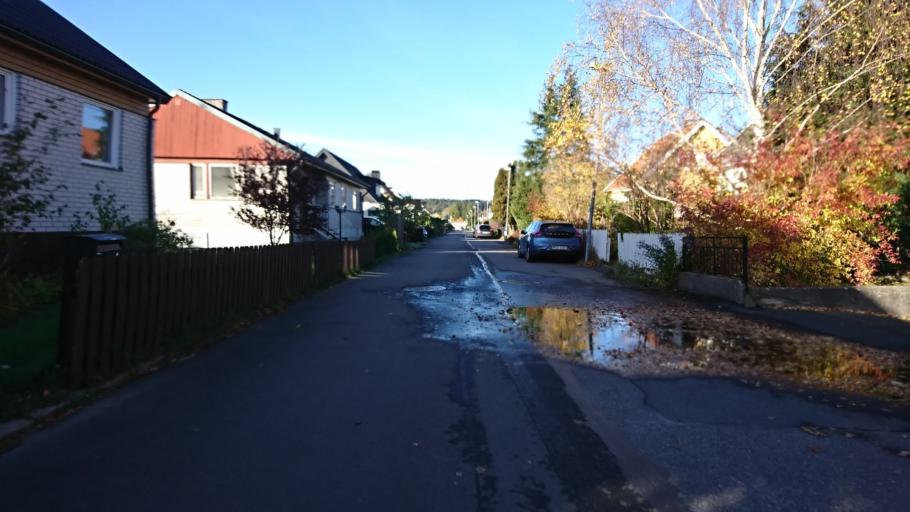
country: SE
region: Vaestra Goetaland
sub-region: Molndal
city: Moelndal
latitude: 57.6548
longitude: 11.9988
